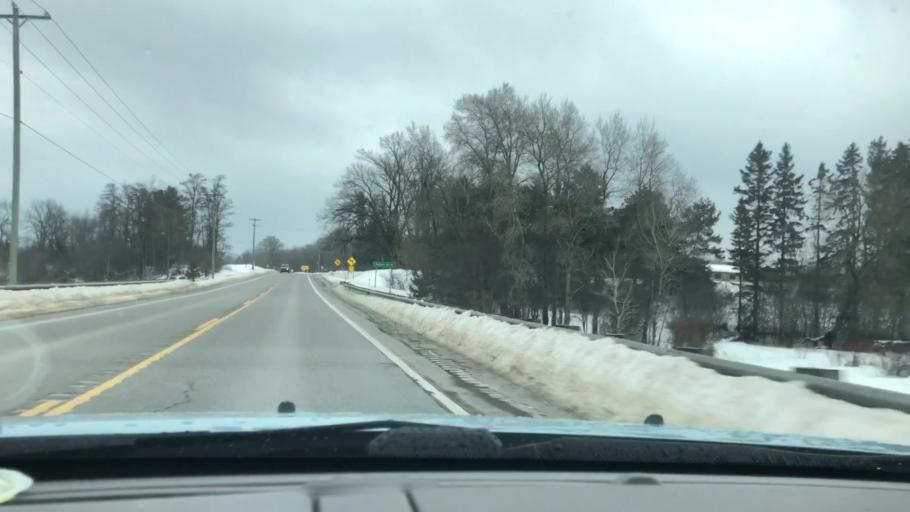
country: US
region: Michigan
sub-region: Charlevoix County
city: East Jordan
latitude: 45.1356
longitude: -85.1192
